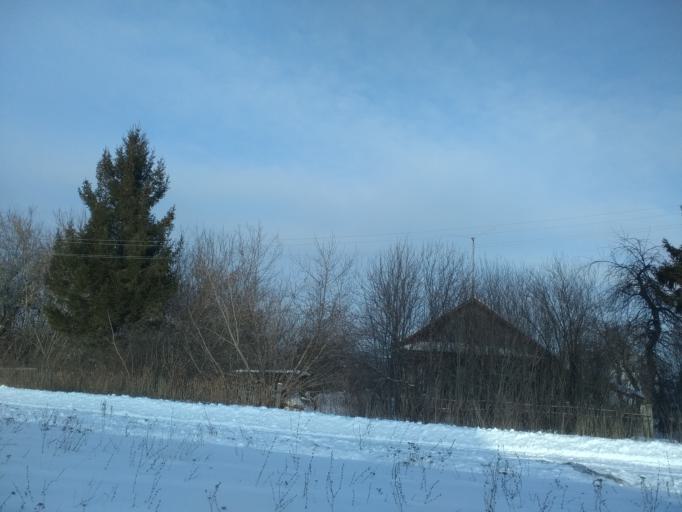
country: RU
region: Bashkortostan
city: Iglino
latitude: 54.6086
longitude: 56.4948
